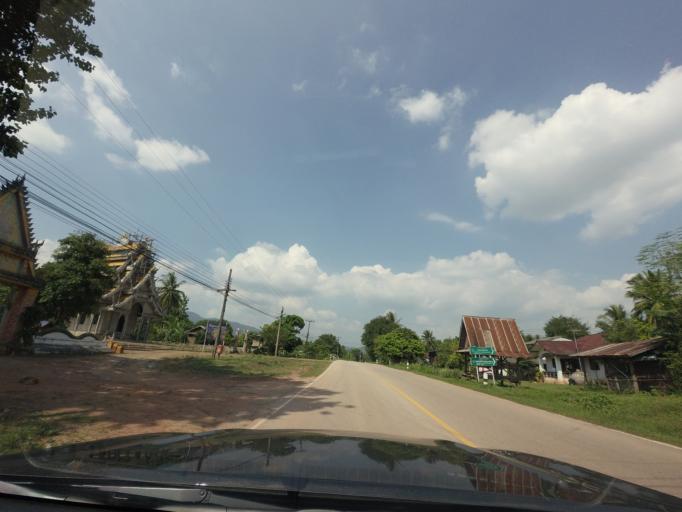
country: TH
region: Uttaradit
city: Ban Khok
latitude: 18.0041
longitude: 101.0354
